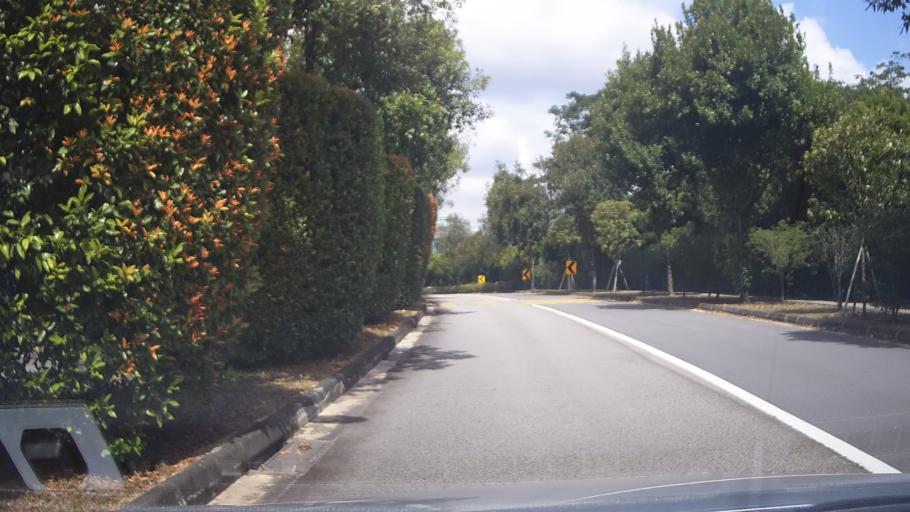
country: SG
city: Singapore
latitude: 1.3218
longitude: 103.7594
